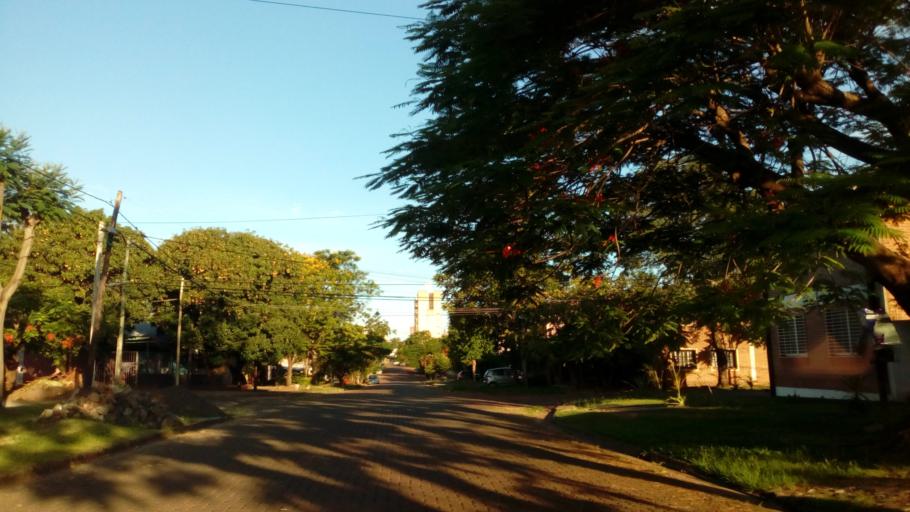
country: AR
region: Misiones
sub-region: Departamento de Capital
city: Posadas
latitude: -27.3678
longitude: -55.9117
